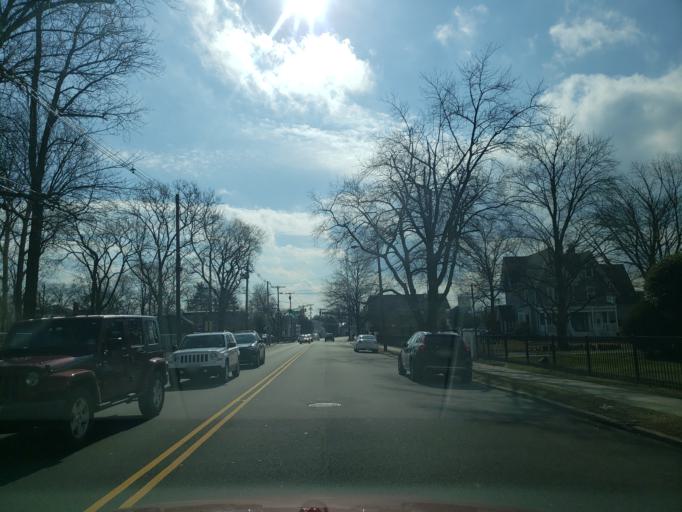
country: US
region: New Jersey
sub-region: Union County
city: Springfield
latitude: 40.7215
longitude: -74.3069
